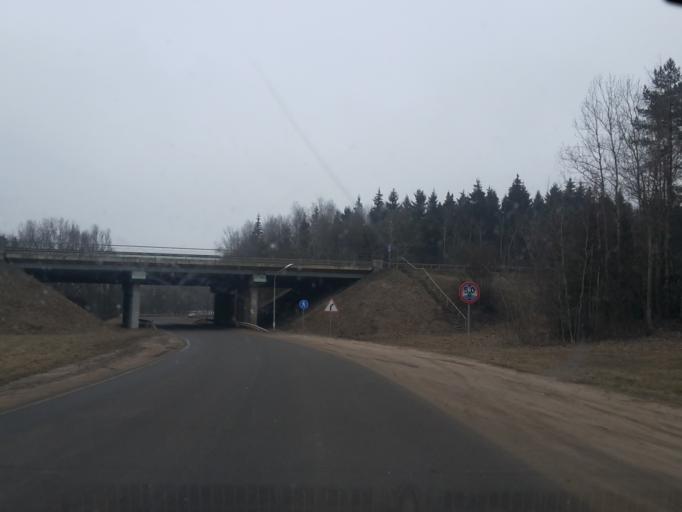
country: BY
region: Minsk
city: Zhdanovichy
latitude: 53.9110
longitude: 27.3912
